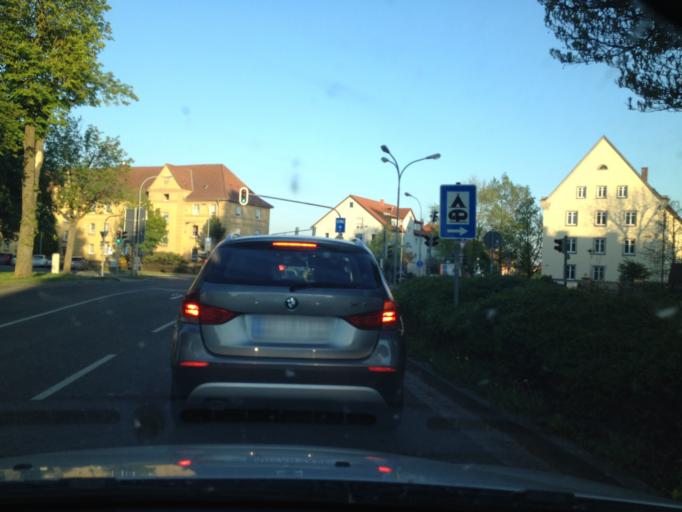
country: DE
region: Bavaria
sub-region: Regierungsbezirk Mittelfranken
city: Rothenburg ob der Tauber
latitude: 49.3805
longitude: 10.1859
